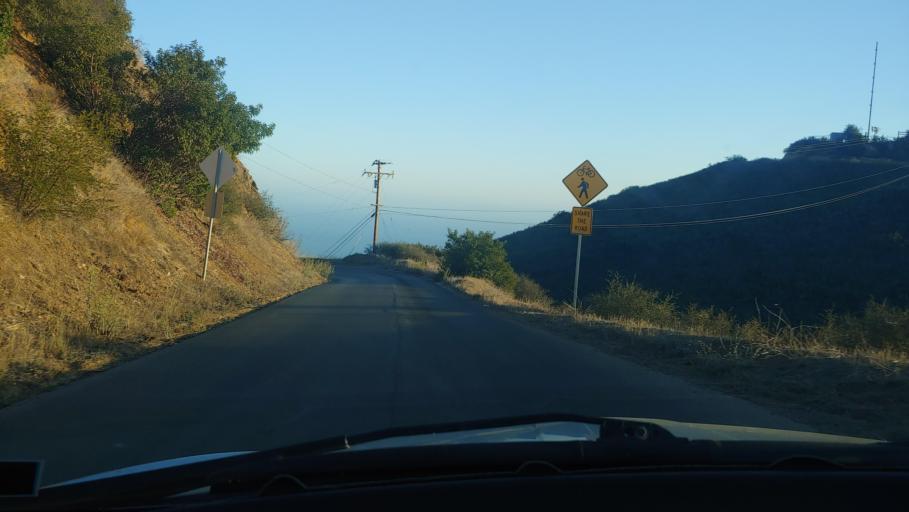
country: US
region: California
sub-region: Santa Barbara County
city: Mission Canyon
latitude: 34.4683
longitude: -119.6773
